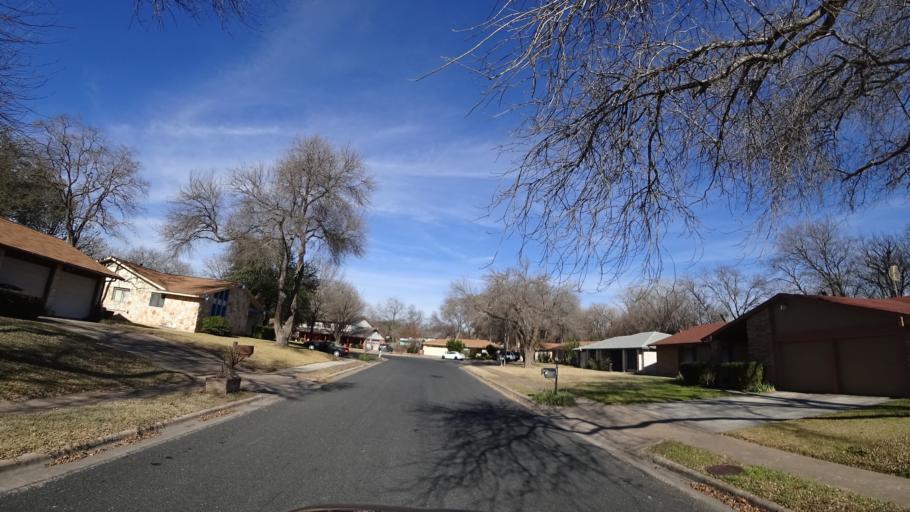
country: US
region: Texas
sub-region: Travis County
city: Wells Branch
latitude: 30.3766
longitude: -97.7022
